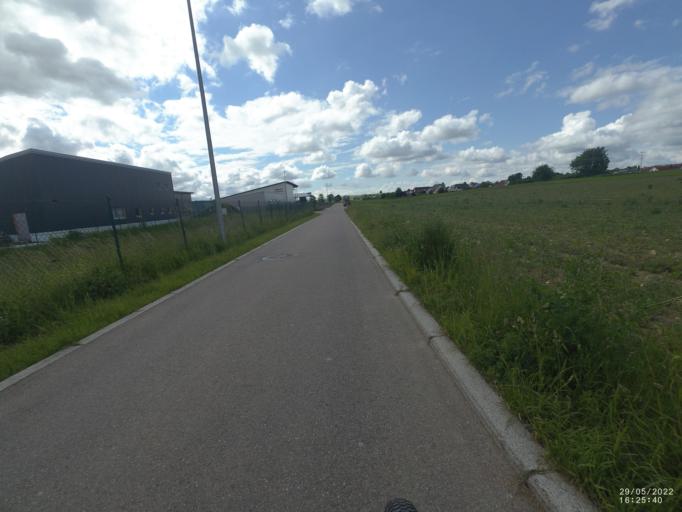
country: DE
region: Baden-Wuerttemberg
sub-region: Regierungsbezirk Stuttgart
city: Bolheim
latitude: 48.5925
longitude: 10.1219
